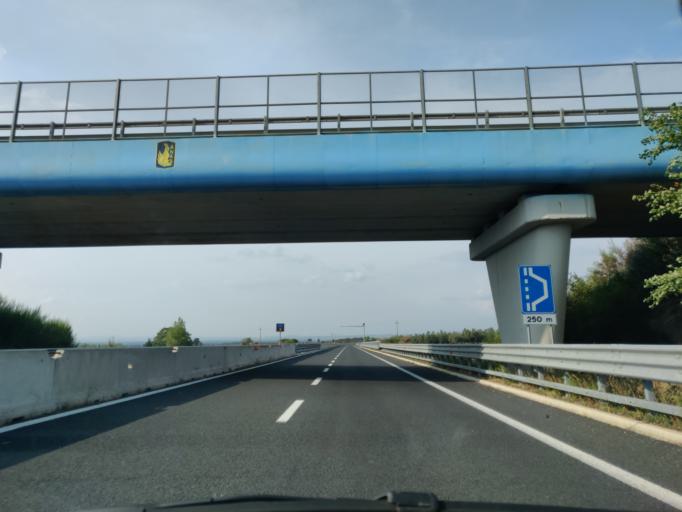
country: IT
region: Latium
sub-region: Provincia di Viterbo
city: Blera
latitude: 42.3443
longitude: 11.9821
